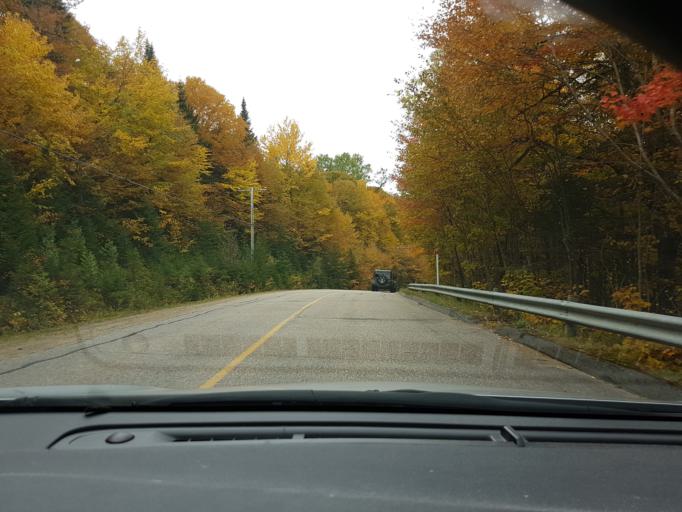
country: CA
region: Quebec
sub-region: Capitale-Nationale
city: Shannon
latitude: 47.1094
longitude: -71.3598
